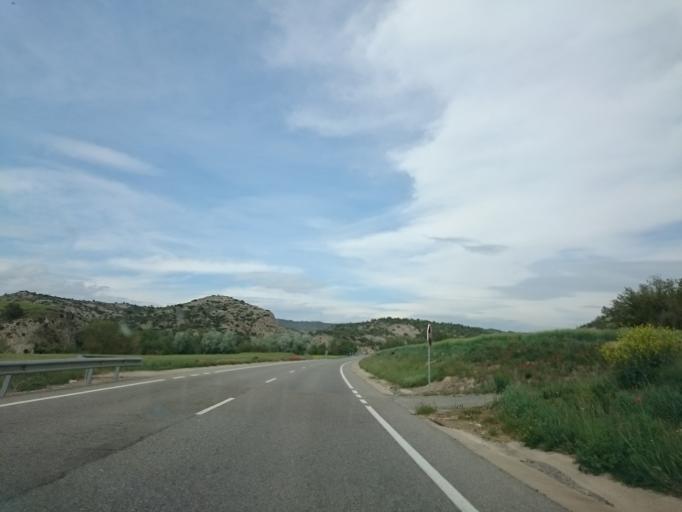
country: ES
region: Catalonia
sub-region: Provincia de Lleida
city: Tora de Riubregos
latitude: 41.8225
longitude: 1.3256
